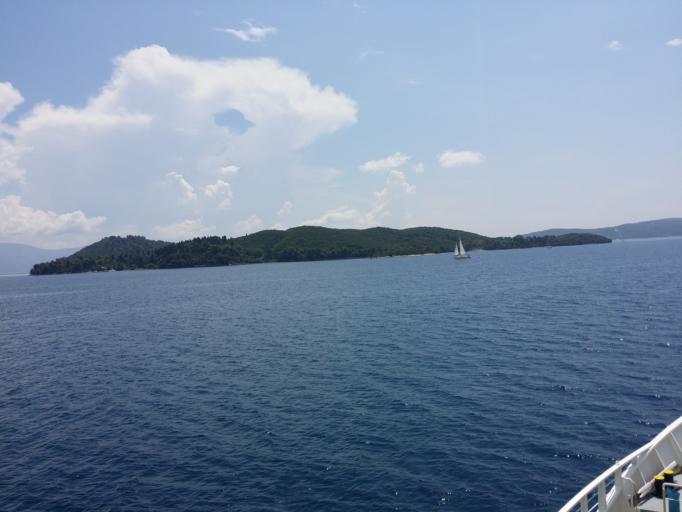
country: GR
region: Ionian Islands
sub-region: Lefkada
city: Nidri
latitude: 38.6967
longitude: 20.7271
